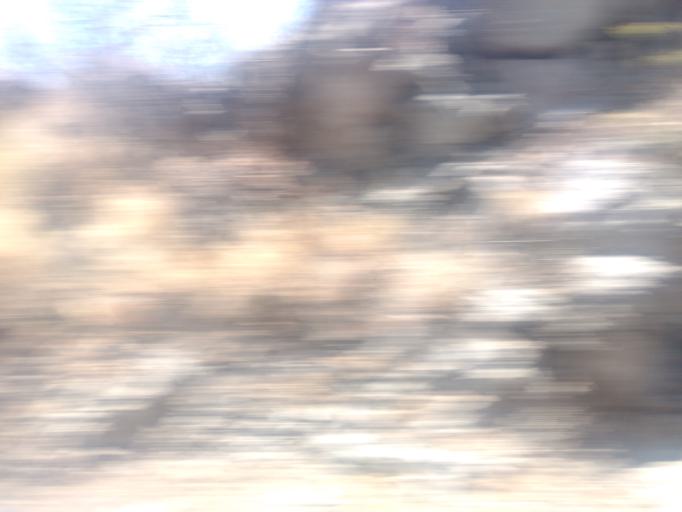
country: MX
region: Jalisco
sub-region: Tonila
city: San Marcos
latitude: 19.5013
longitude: -103.4433
